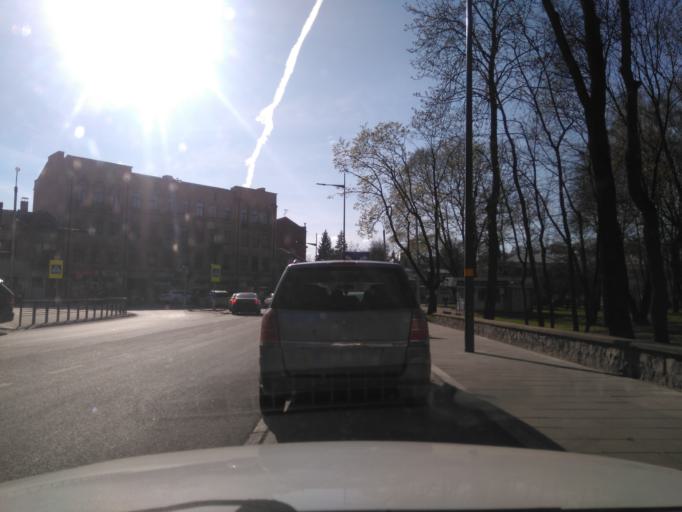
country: LT
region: Kauno apskritis
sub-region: Kaunas
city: Aleksotas
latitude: 54.8902
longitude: 23.9264
